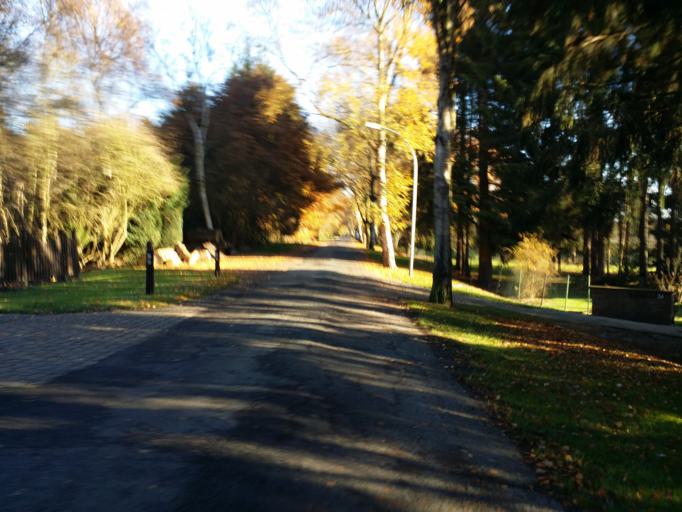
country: DE
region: Lower Saxony
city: Oyten
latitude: 53.0724
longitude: 8.9853
